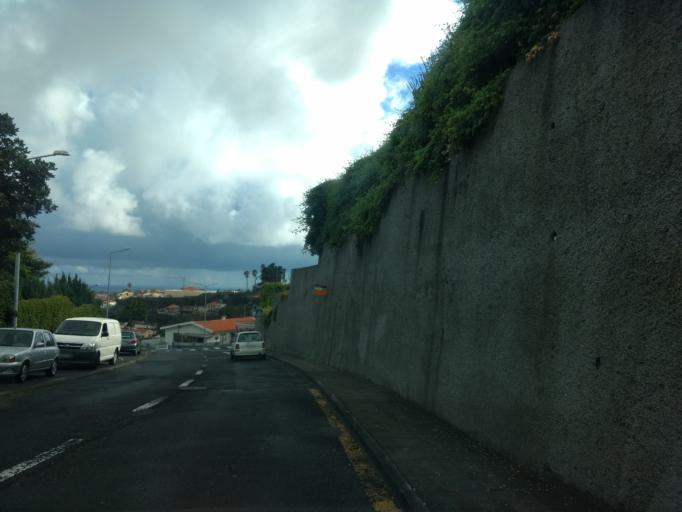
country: PT
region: Madeira
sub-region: Funchal
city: Nossa Senhora do Monte
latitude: 32.6592
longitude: -16.9154
